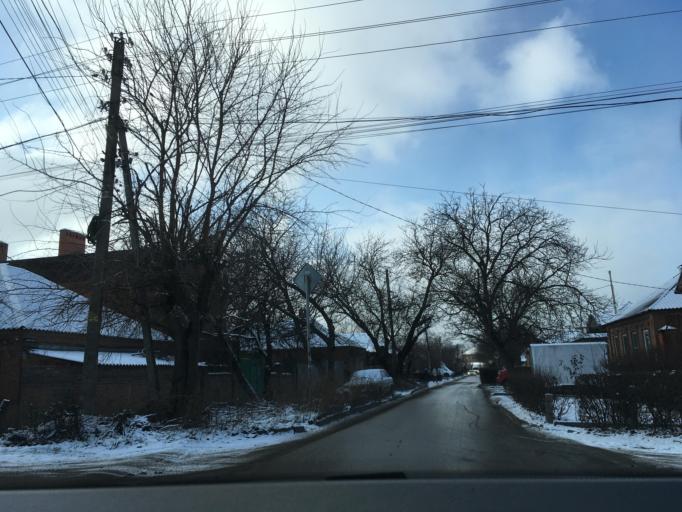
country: RU
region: Rostov
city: Rostov-na-Donu
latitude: 47.2341
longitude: 39.6325
